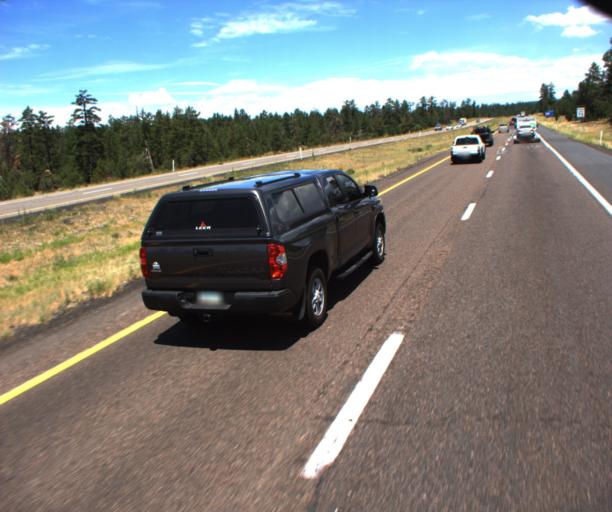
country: US
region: Arizona
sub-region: Coconino County
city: Sedona
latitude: 34.9223
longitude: -111.6443
